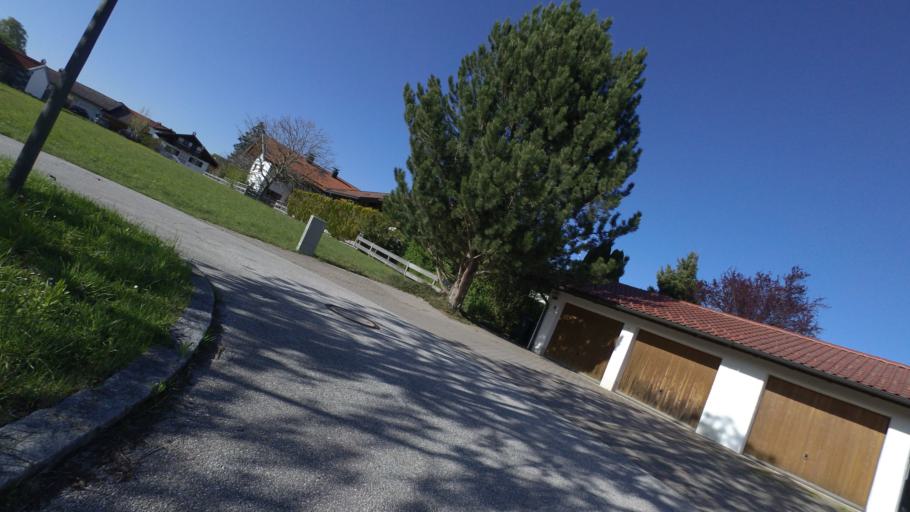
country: DE
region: Bavaria
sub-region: Upper Bavaria
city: Grabenstatt
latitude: 47.8558
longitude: 12.5387
